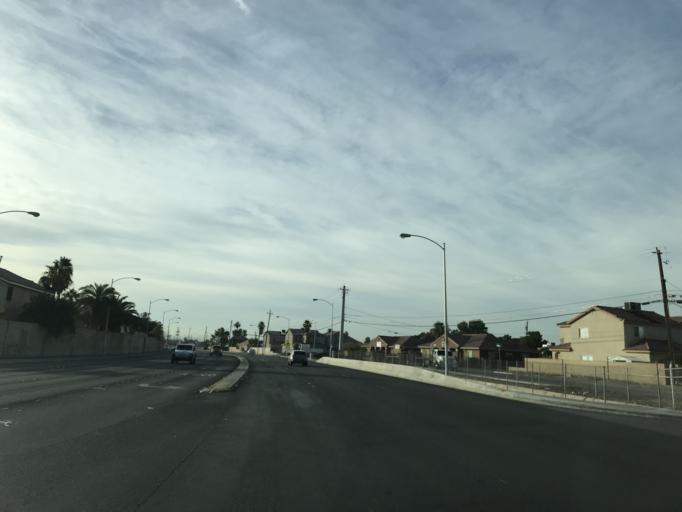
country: US
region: Nevada
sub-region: Clark County
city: Winchester
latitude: 36.1520
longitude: -115.0651
